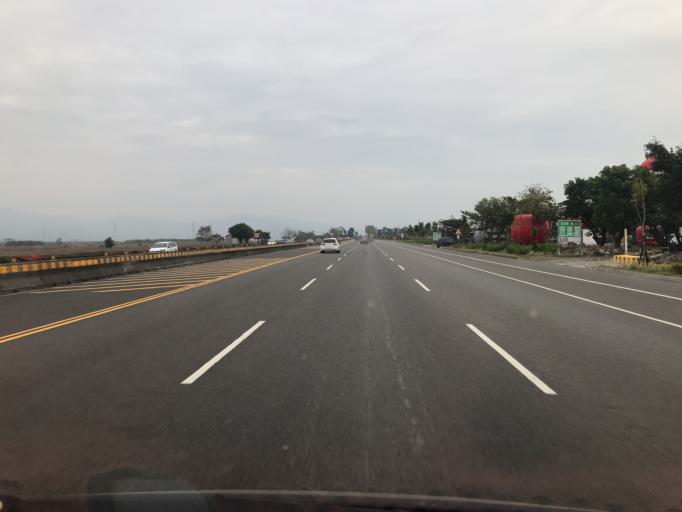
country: TW
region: Taiwan
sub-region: Pingtung
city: Pingtung
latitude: 22.4243
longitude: 120.5793
